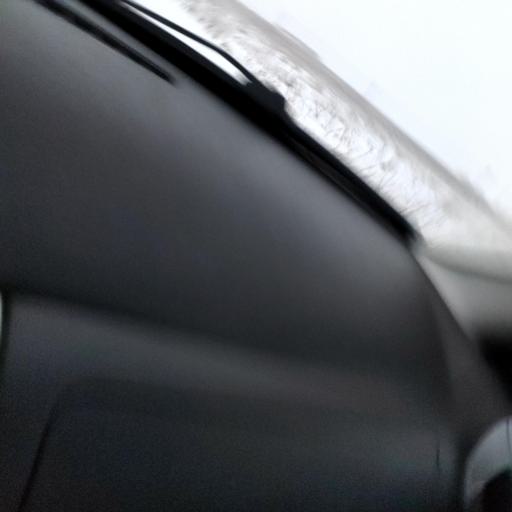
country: RU
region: Bashkortostan
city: Ulukulevo
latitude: 54.3997
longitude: 56.4428
